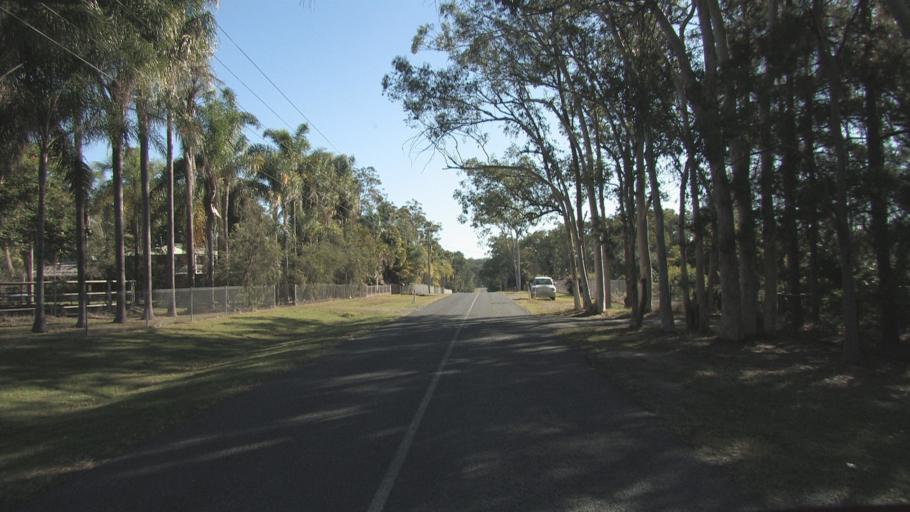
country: AU
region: Queensland
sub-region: Logan
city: Logan Reserve
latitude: -27.7395
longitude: 153.0934
